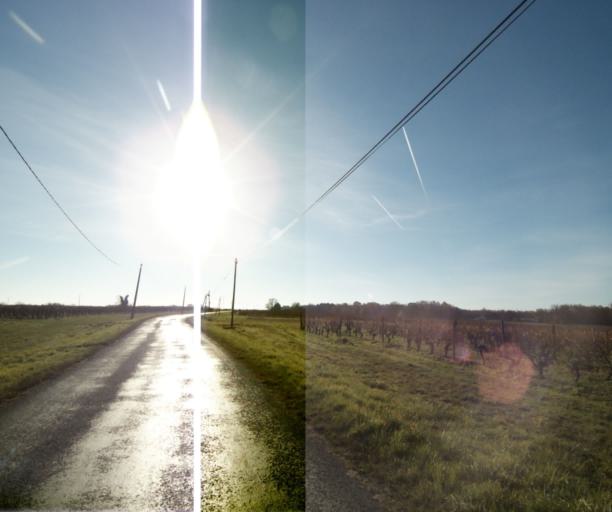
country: FR
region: Poitou-Charentes
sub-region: Departement de la Charente-Maritime
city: Cherac
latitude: 45.7207
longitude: -0.4540
